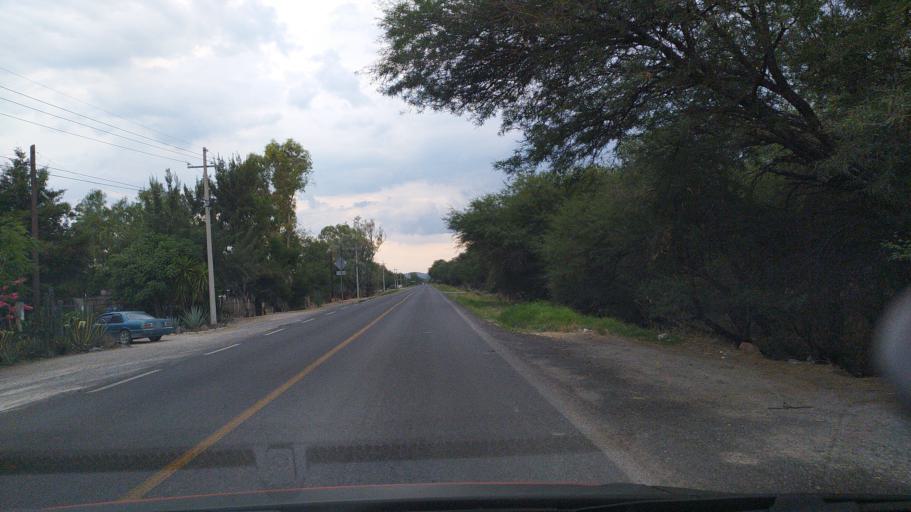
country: MX
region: Guanajuato
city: San Roque
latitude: 20.9736
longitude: -101.8549
